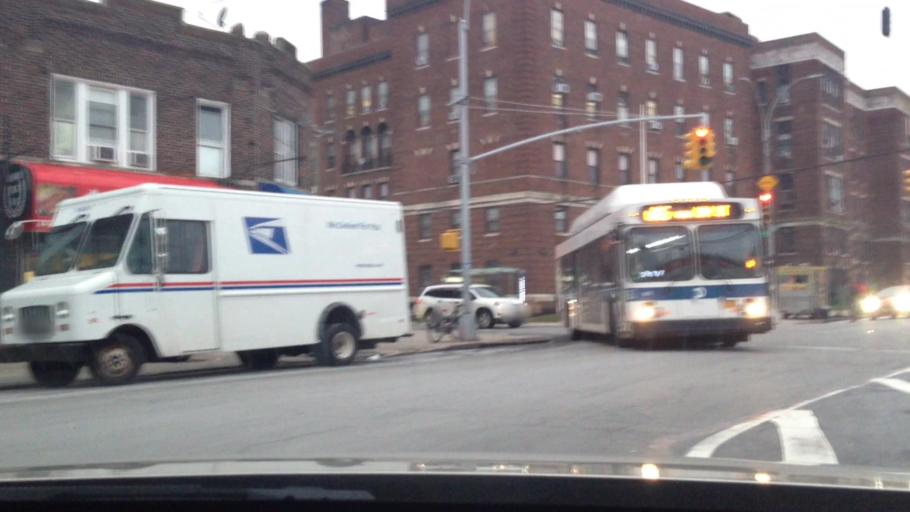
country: US
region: New York
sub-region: Queens County
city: Jamaica
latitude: 40.7555
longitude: -73.8153
